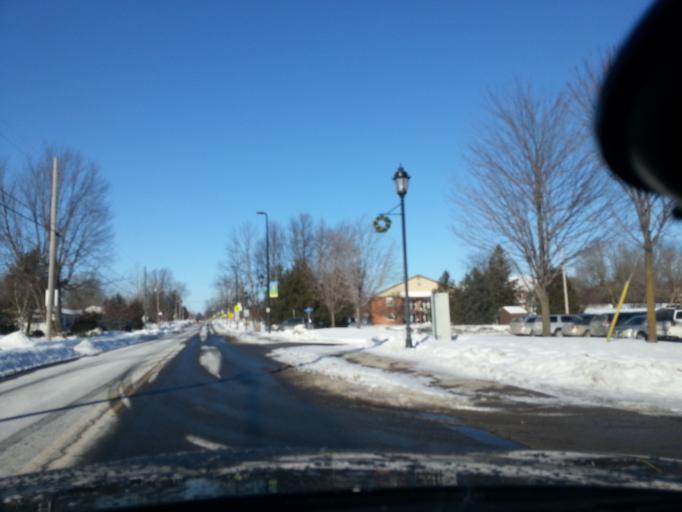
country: CA
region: Ontario
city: Ottawa
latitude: 45.2298
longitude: -75.4696
